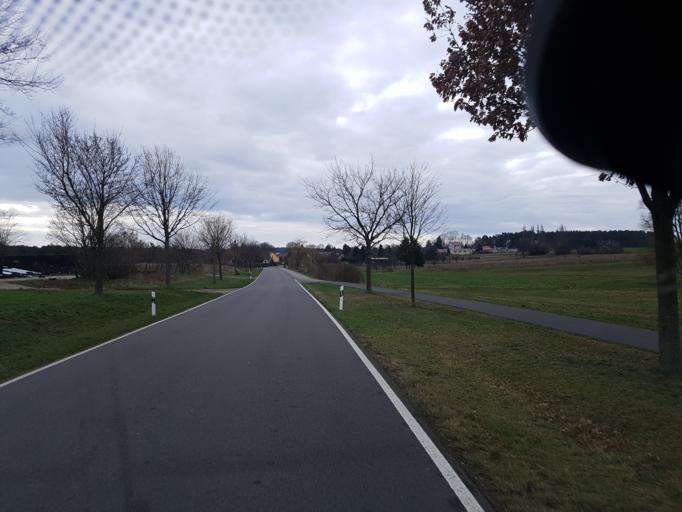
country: DE
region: Brandenburg
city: Gross Lindow
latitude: 52.1486
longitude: 14.5253
